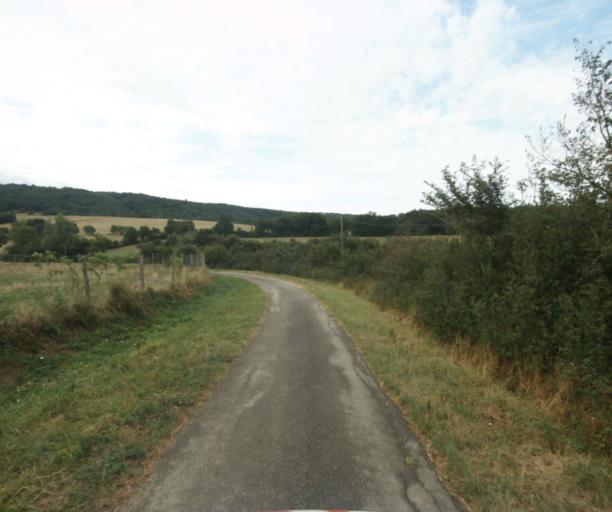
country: FR
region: Midi-Pyrenees
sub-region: Departement de la Haute-Garonne
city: Revel
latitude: 43.4262
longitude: 1.9975
